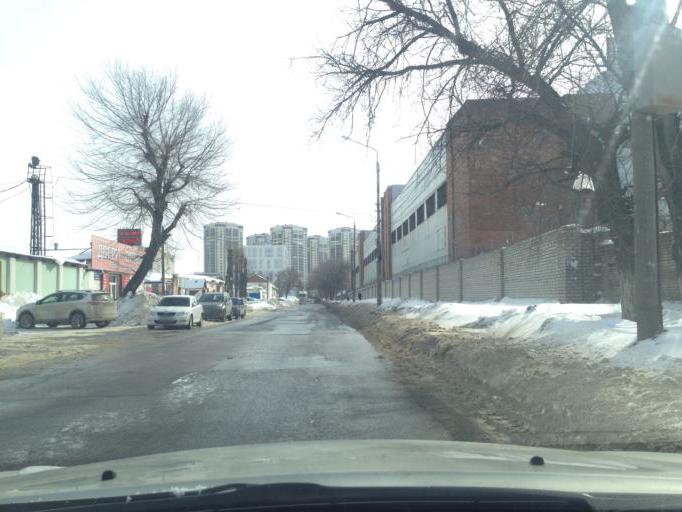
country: RU
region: Voronezj
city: Voronezh
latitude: 51.6600
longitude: 39.1741
